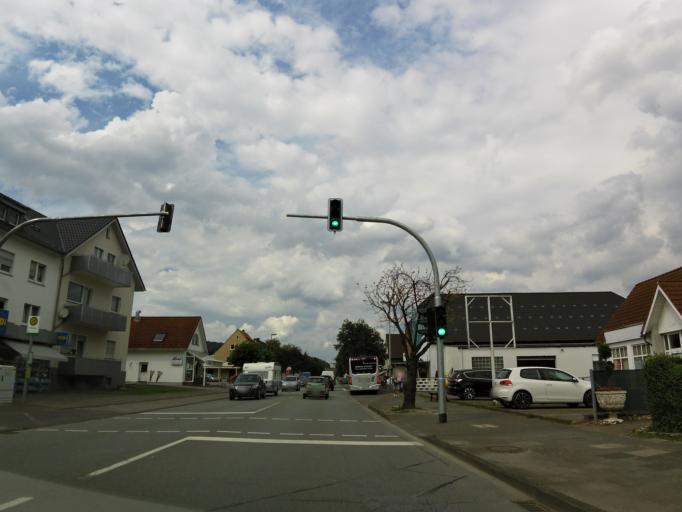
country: DE
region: North Rhine-Westphalia
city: Beverungen
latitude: 51.6688
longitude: 9.3748
